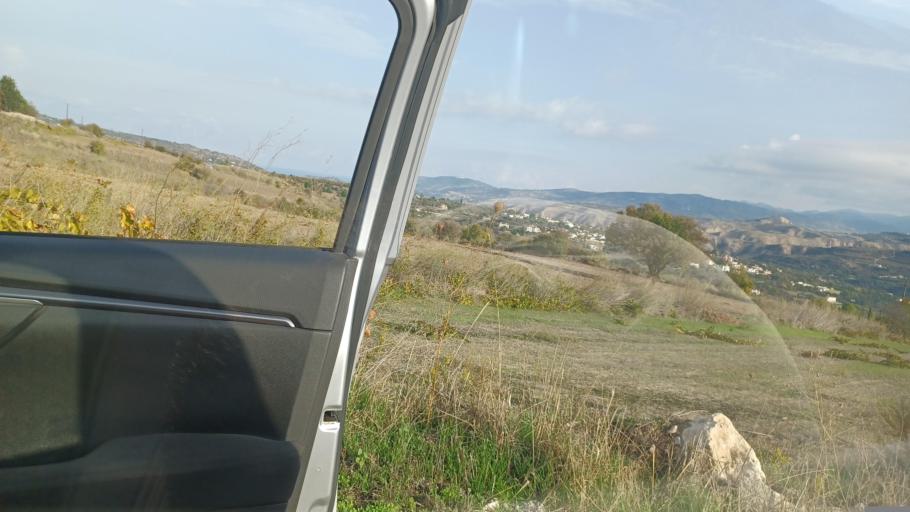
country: CY
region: Pafos
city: Tala
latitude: 34.9100
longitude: 32.4693
